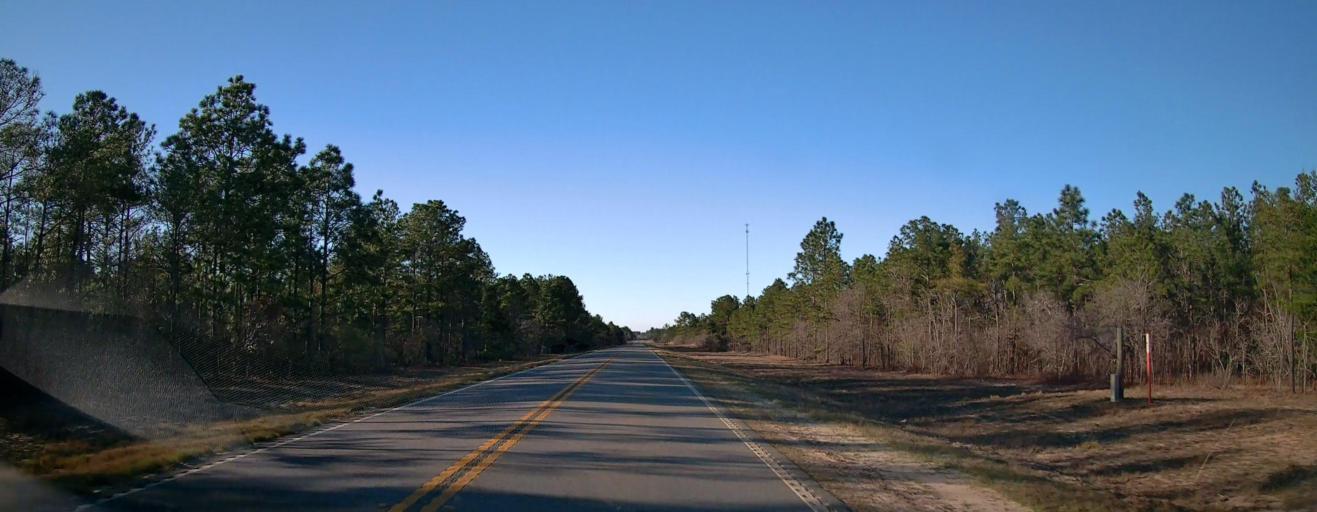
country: US
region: Georgia
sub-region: Talbot County
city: Talbotton
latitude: 32.5646
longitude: -84.4383
